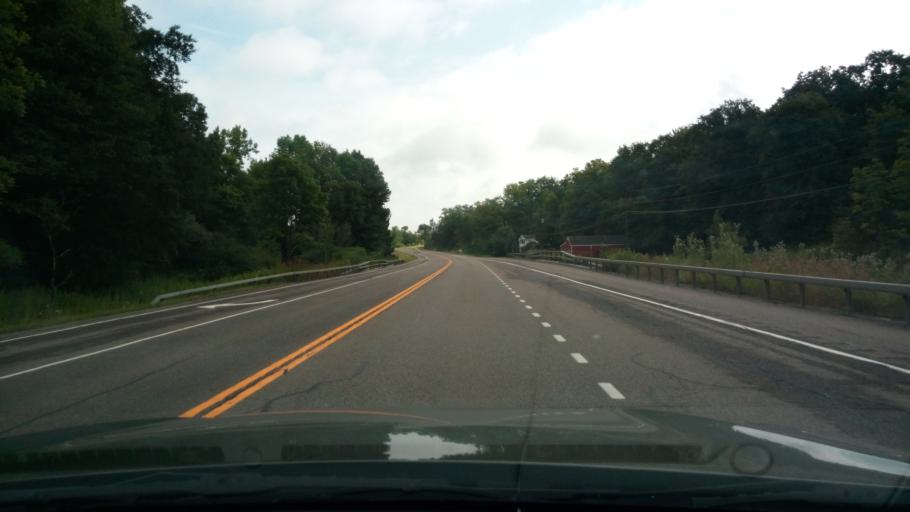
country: US
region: New York
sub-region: Chemung County
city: Horseheads North
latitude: 42.2414
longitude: -76.7557
